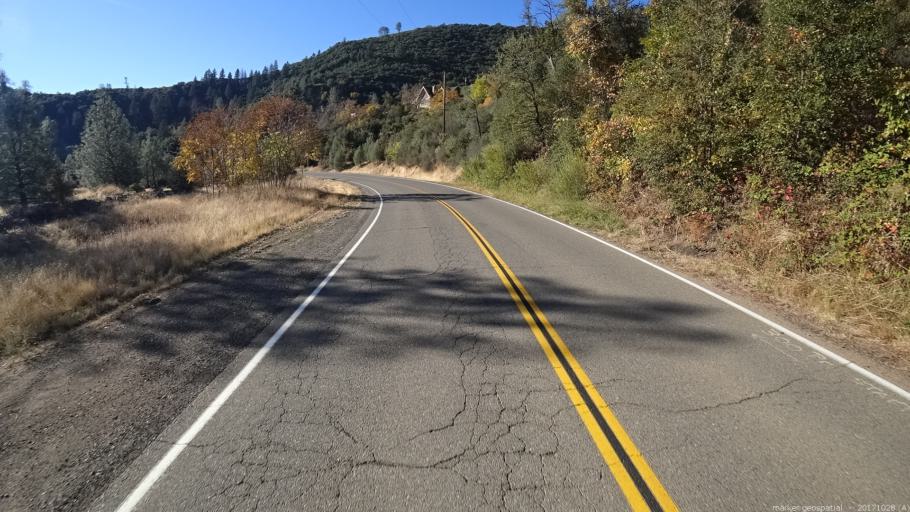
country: US
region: California
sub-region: Trinity County
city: Lewiston
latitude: 40.6816
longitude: -122.6405
